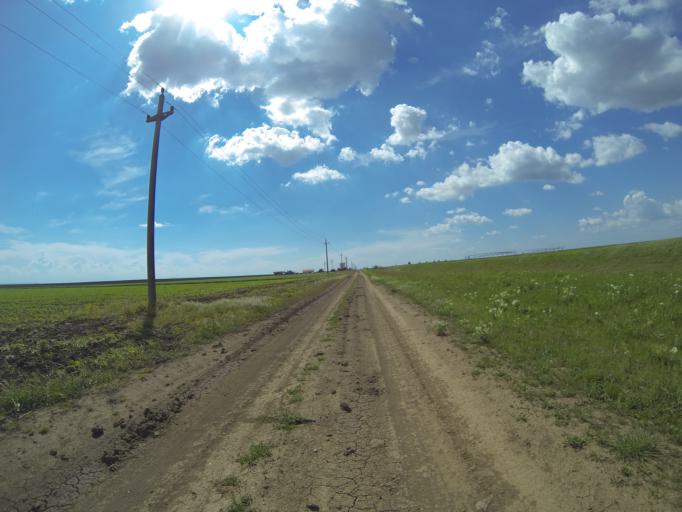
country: RO
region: Dolj
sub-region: Comuna Segarcea
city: Segarcea
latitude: 44.0189
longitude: 23.7656
